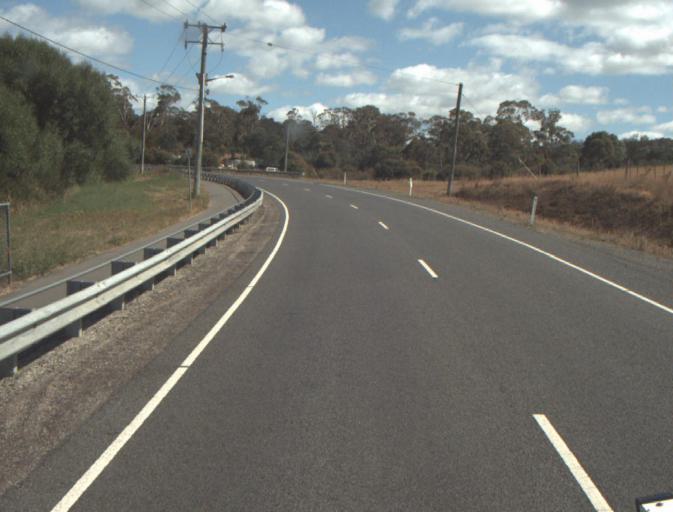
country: AU
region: Tasmania
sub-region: Launceston
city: Newstead
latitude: -41.4268
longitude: 147.1863
